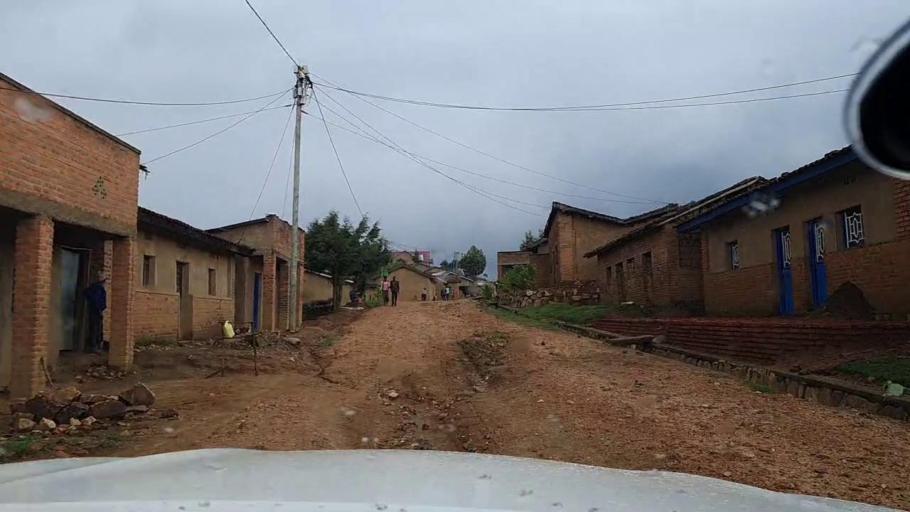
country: RW
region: Western Province
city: Kibuye
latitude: -2.1082
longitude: 29.4842
